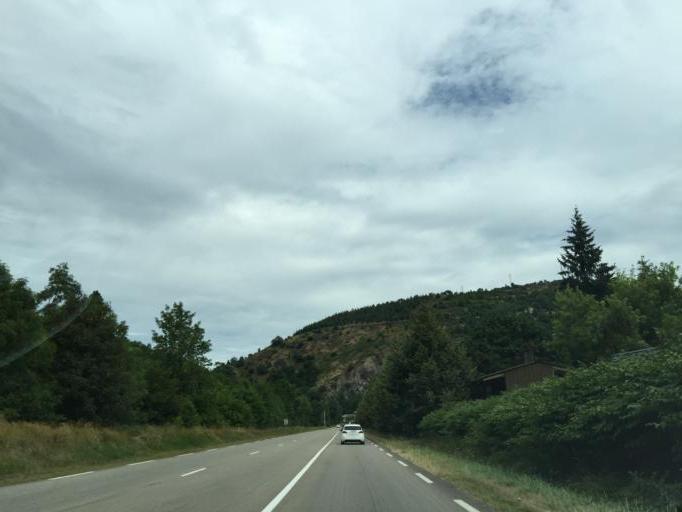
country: FR
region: Rhone-Alpes
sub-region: Departement de la Loire
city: Fraisses
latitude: 45.4037
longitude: 4.2546
